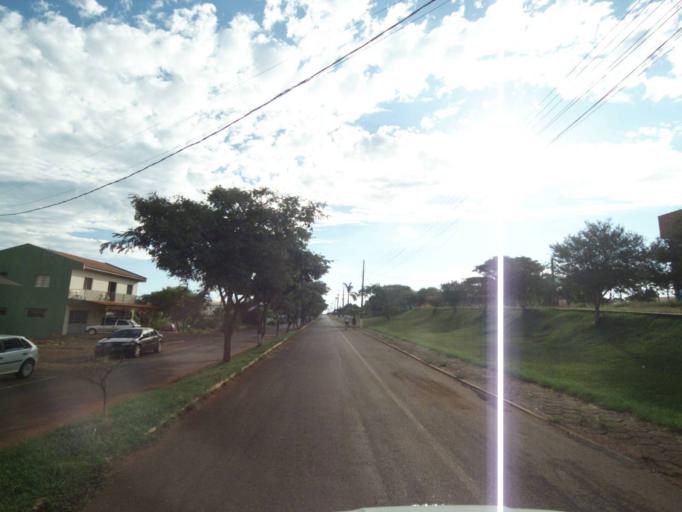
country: BR
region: Parana
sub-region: Laranjeiras Do Sul
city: Laranjeiras do Sul
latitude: -25.4930
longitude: -52.5305
